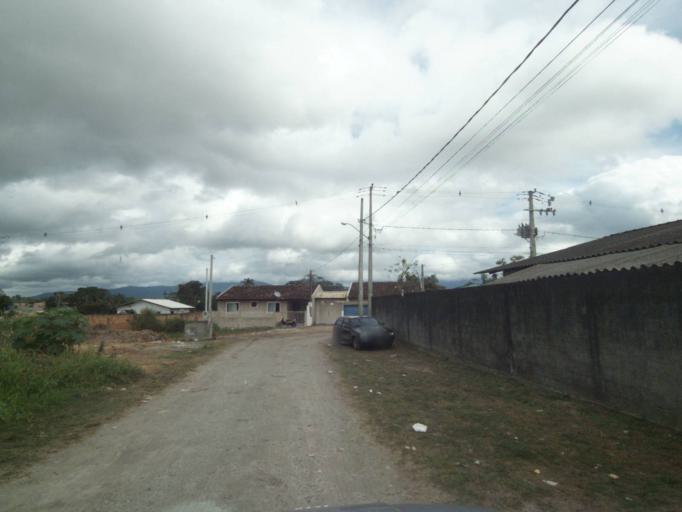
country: BR
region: Parana
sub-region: Paranagua
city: Paranagua
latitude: -25.5717
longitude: -48.5627
